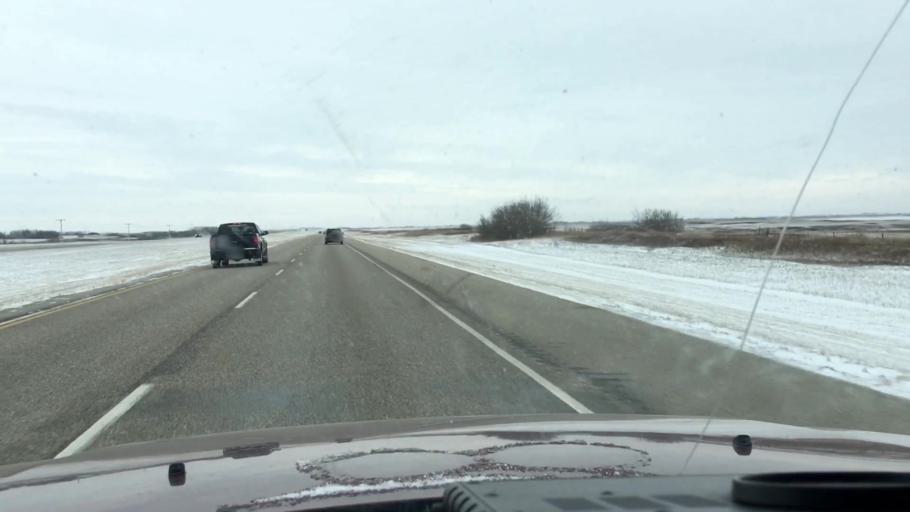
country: CA
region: Saskatchewan
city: Saskatoon
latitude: 51.6041
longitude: -106.4031
